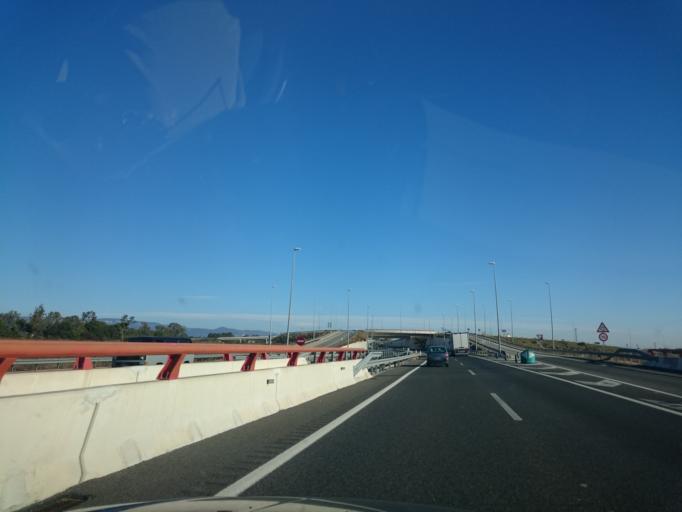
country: ES
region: Catalonia
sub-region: Provincia de Tarragona
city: Cambrils
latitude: 41.0556
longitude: 0.9874
